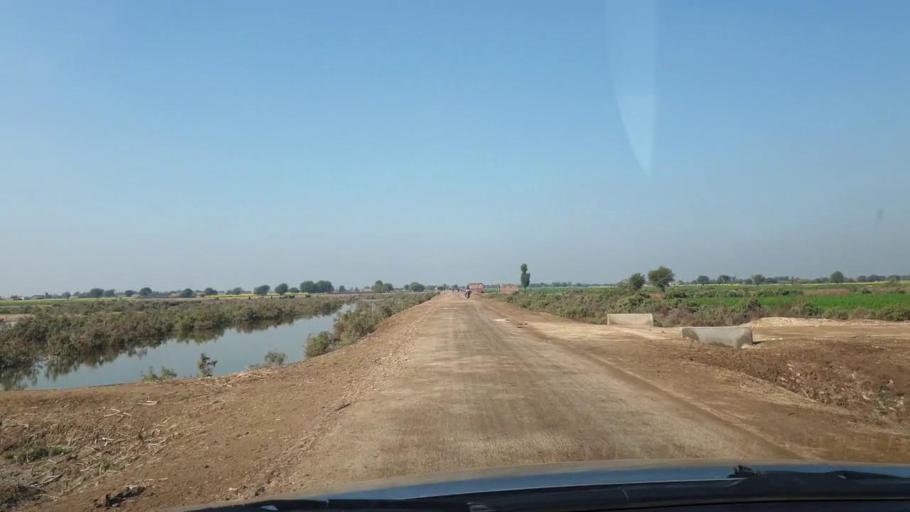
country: PK
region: Sindh
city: Jhol
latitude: 25.8807
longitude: 68.9186
